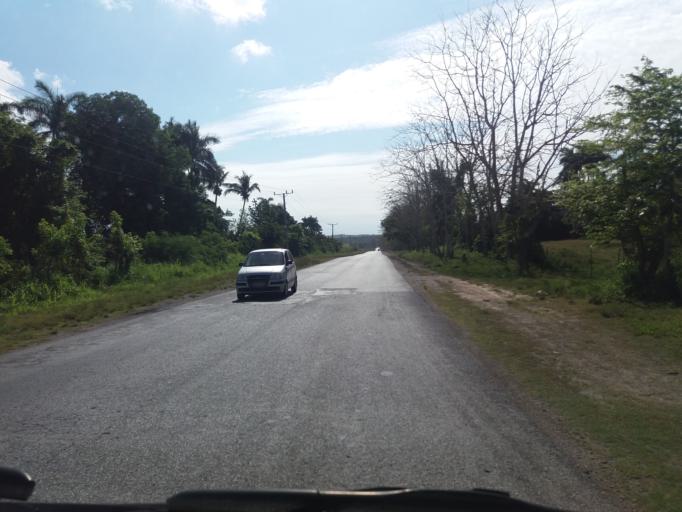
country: CU
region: Cienfuegos
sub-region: Municipio de Cienfuegos
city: Cienfuegos
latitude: 22.1656
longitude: -80.3831
